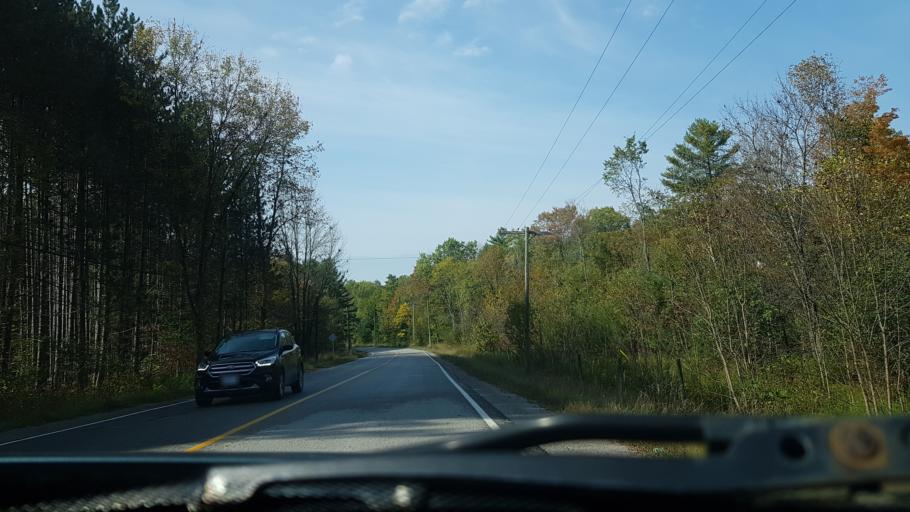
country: CA
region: Ontario
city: Gravenhurst
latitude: 44.7751
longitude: -79.3000
